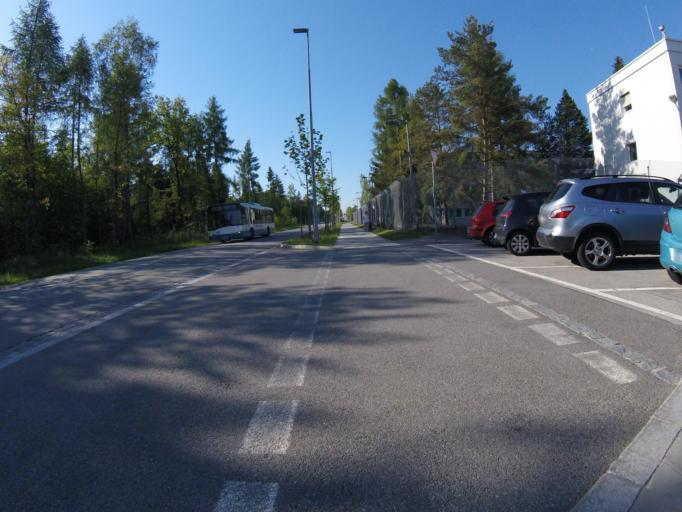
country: DE
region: Bavaria
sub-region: Upper Bavaria
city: Ottobrunn
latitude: 48.0478
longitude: 11.6579
